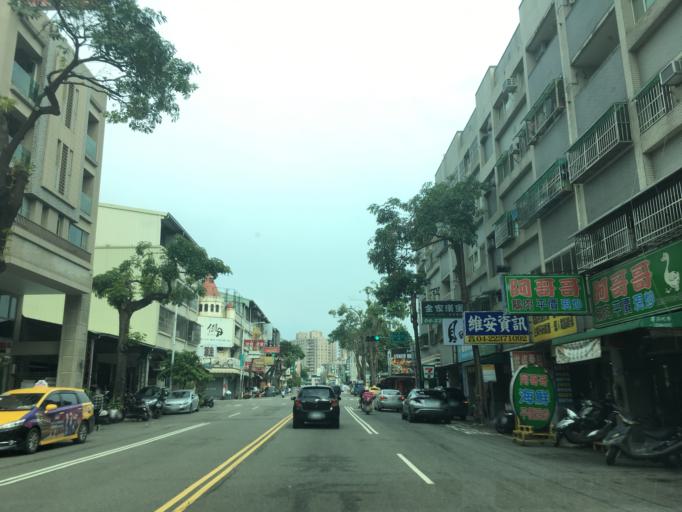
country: TW
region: Taiwan
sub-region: Taichung City
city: Taichung
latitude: 24.1669
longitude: 120.6861
